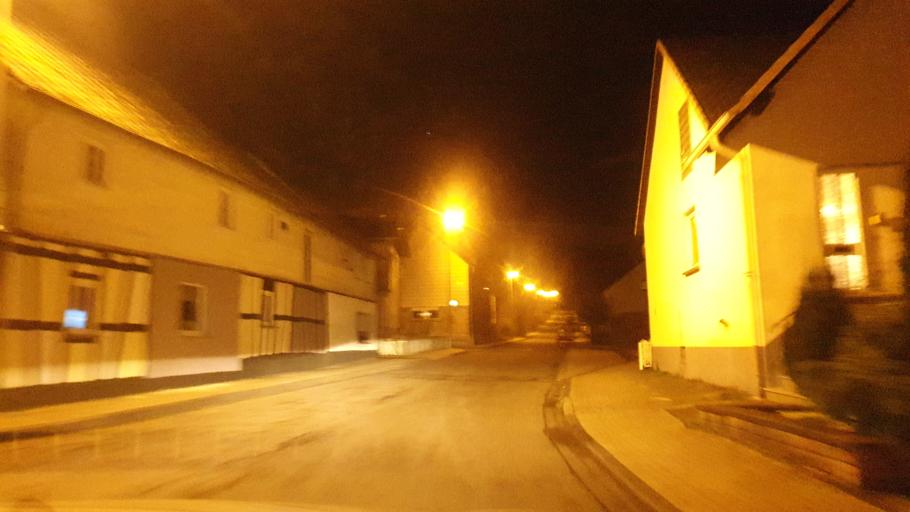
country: DE
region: Rheinland-Pfalz
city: Oberdreis
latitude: 50.6385
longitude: 7.6489
